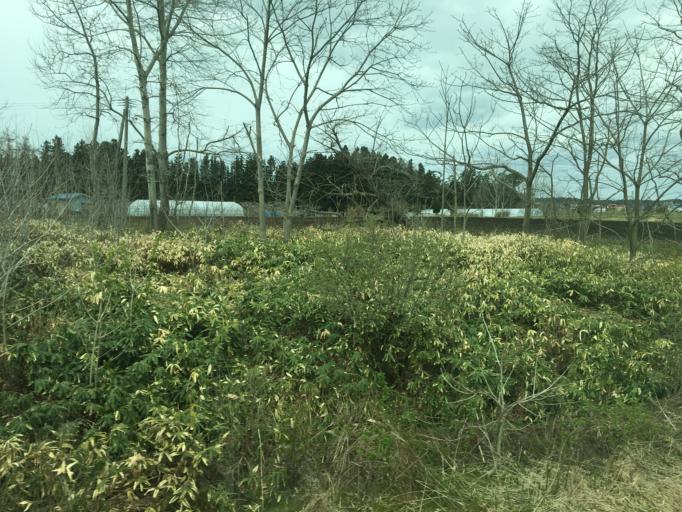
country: JP
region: Aomori
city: Shimokizukuri
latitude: 40.7862
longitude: 140.2929
